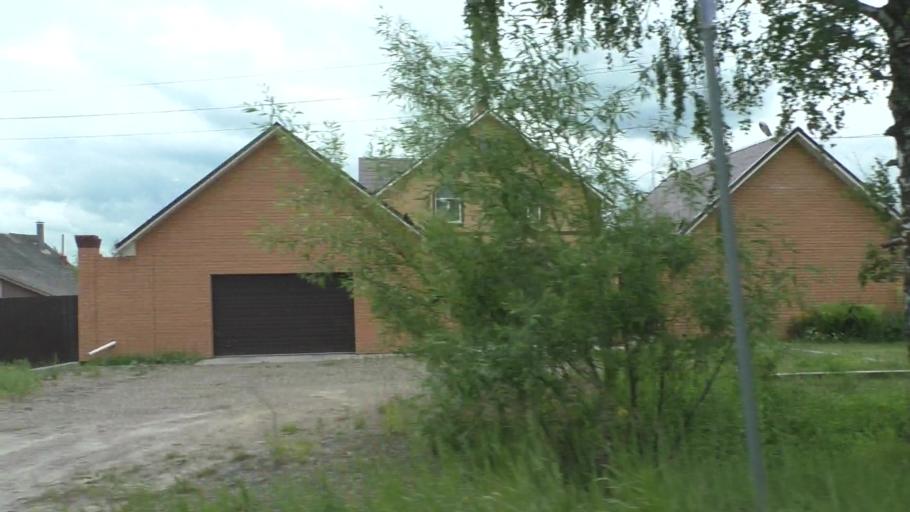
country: RU
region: Moskovskaya
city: Yegor'yevsk
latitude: 55.3989
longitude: 39.0117
